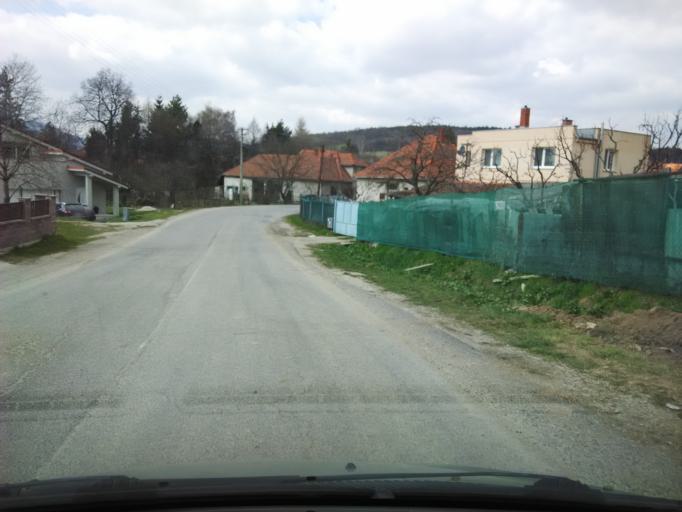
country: SK
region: Nitriansky
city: Zlate Moravce
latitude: 48.4259
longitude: 18.3291
